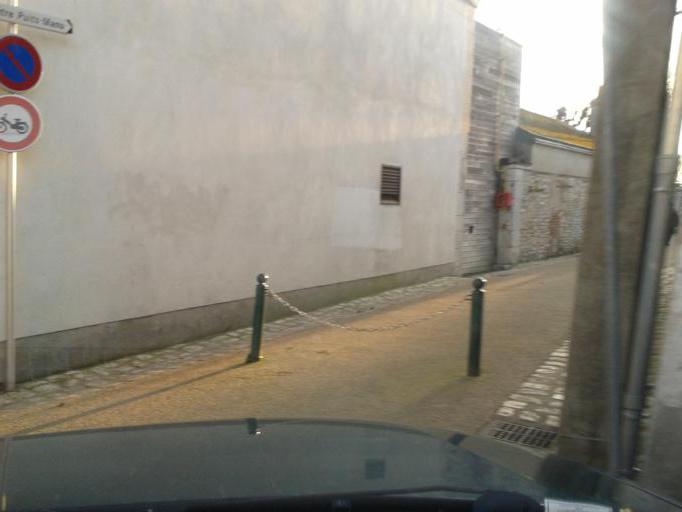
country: FR
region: Centre
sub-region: Departement du Loiret
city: Beaugency
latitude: 47.7761
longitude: 1.6302
